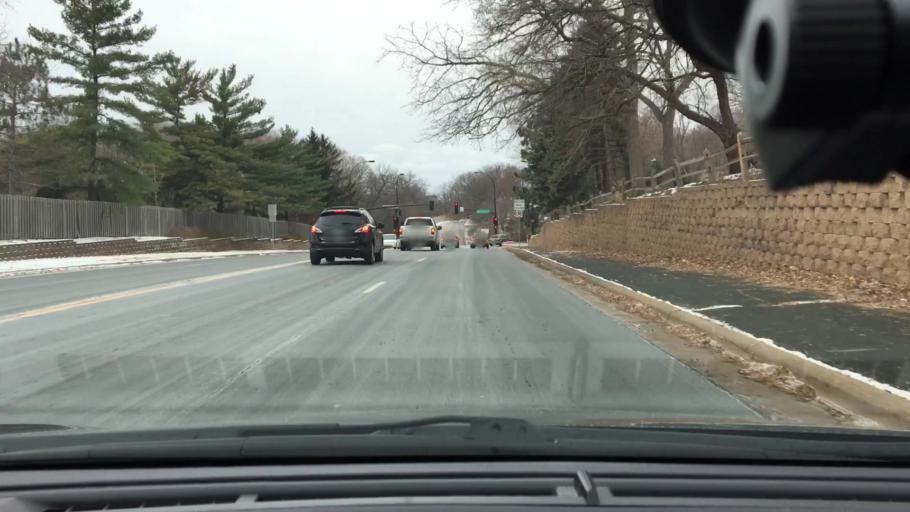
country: US
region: Minnesota
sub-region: Hennepin County
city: Maple Grove
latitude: 45.1091
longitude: -93.4906
